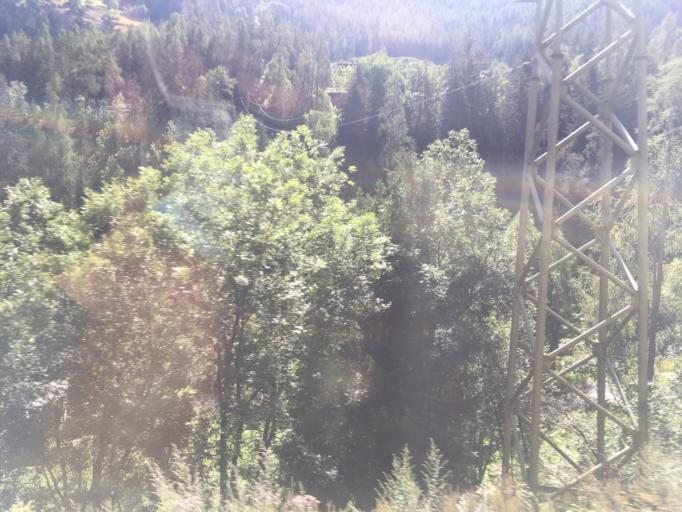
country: CH
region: Valais
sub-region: Visp District
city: Sankt Niklaus
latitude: 46.1609
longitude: 7.7936
